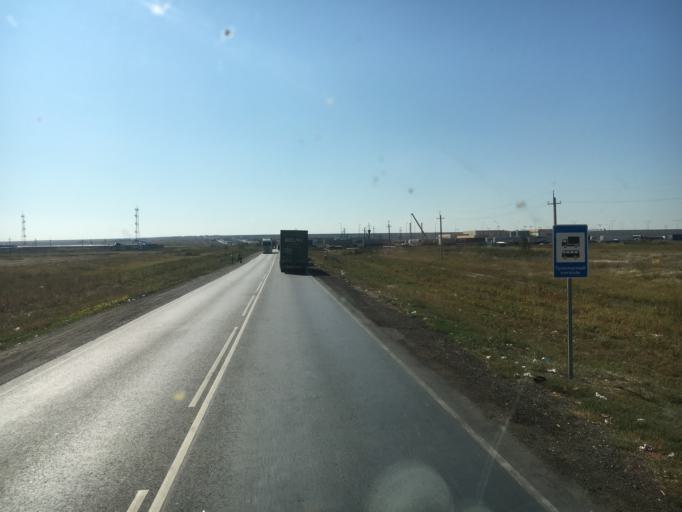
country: KZ
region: Batys Qazaqstan
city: Peremetnoe
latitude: 51.6831
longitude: 51.0031
